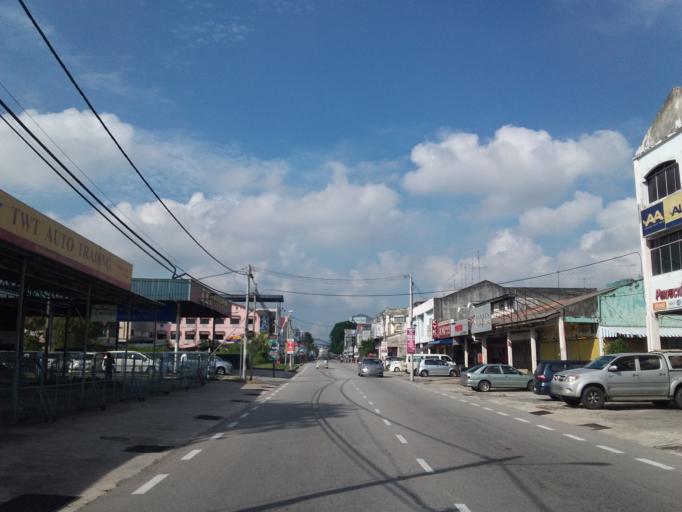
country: MY
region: Johor
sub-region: Daerah Batu Pahat
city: Batu Pahat
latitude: 1.8567
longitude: 102.9299
